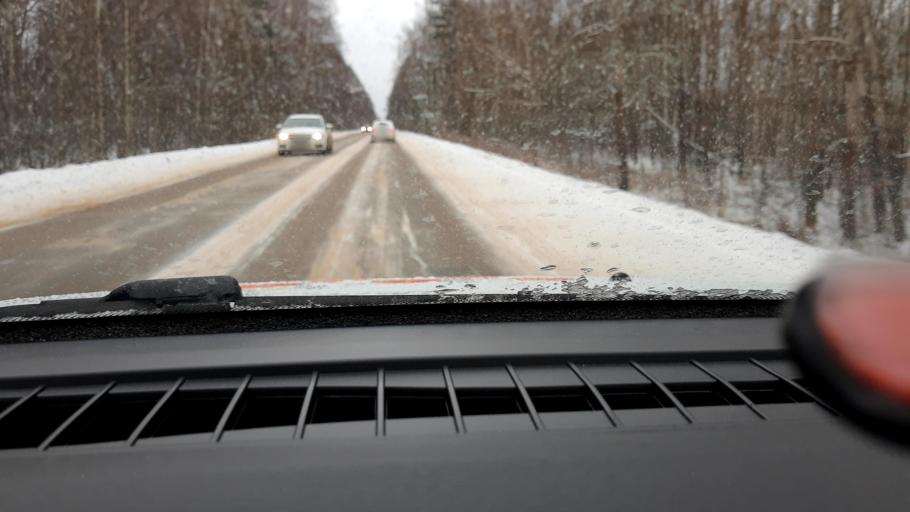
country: RU
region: Nizjnij Novgorod
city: Afonino
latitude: 56.3071
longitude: 44.2427
